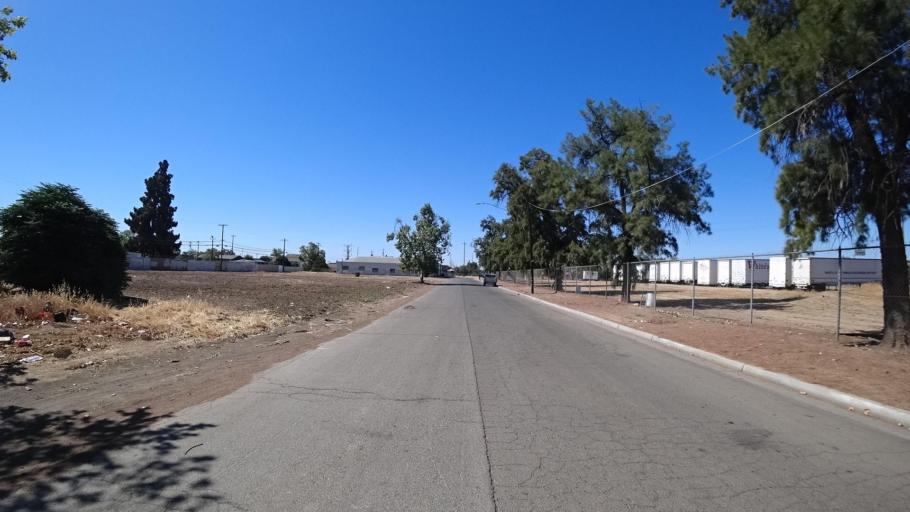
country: US
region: California
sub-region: Fresno County
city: Fresno
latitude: 36.7171
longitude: -119.7818
